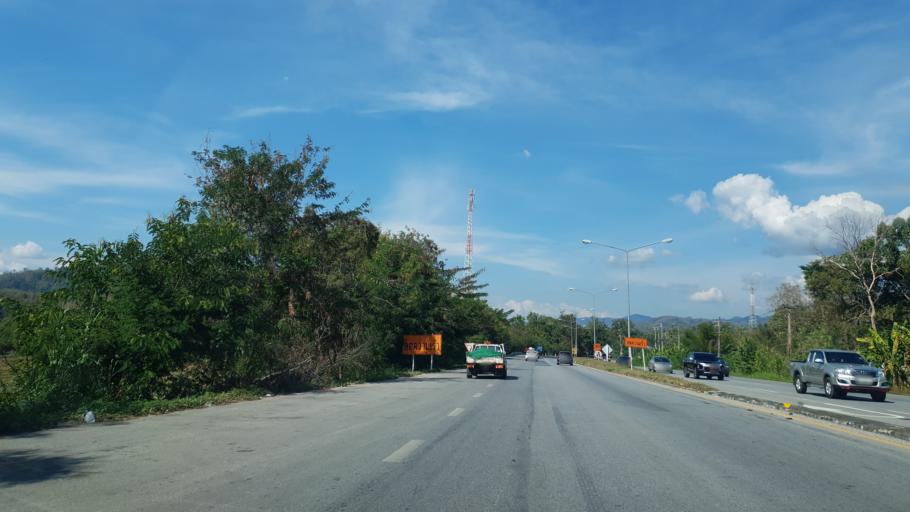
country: TH
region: Uttaradit
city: Uttaradit
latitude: 17.7282
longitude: 100.1329
